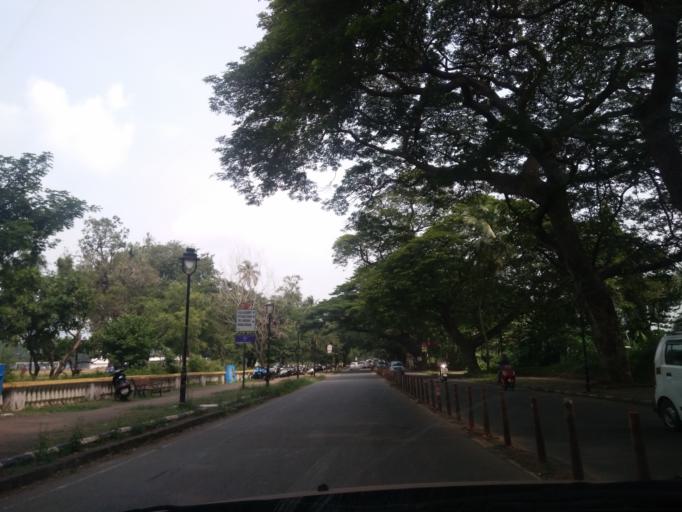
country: IN
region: Goa
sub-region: North Goa
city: Panaji
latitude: 15.4886
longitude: 73.8138
